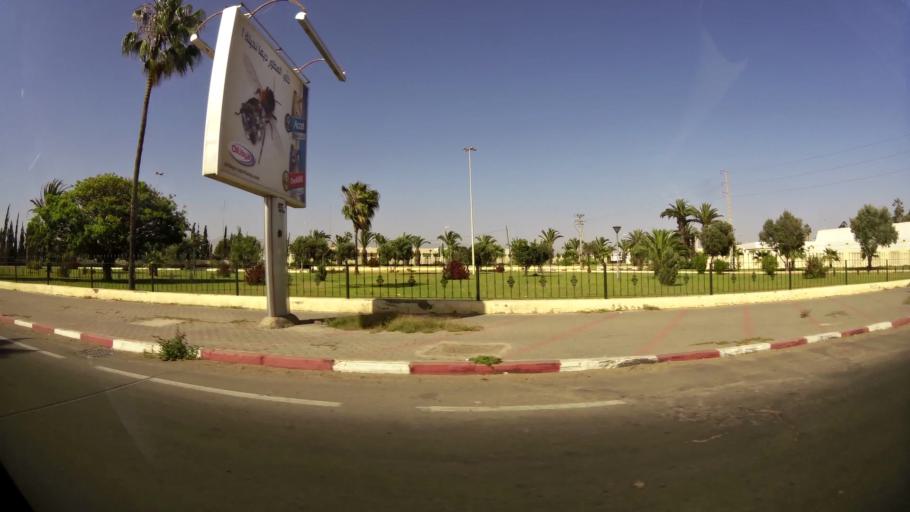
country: MA
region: Oued ed Dahab-Lagouira
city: Dakhla
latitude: 30.3793
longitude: -9.5622
